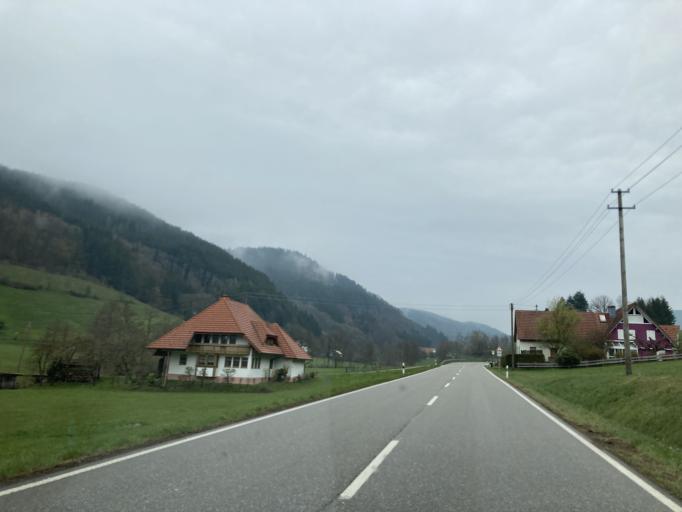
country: DE
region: Baden-Wuerttemberg
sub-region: Freiburg Region
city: Muhlenbach
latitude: 48.2007
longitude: 8.1156
